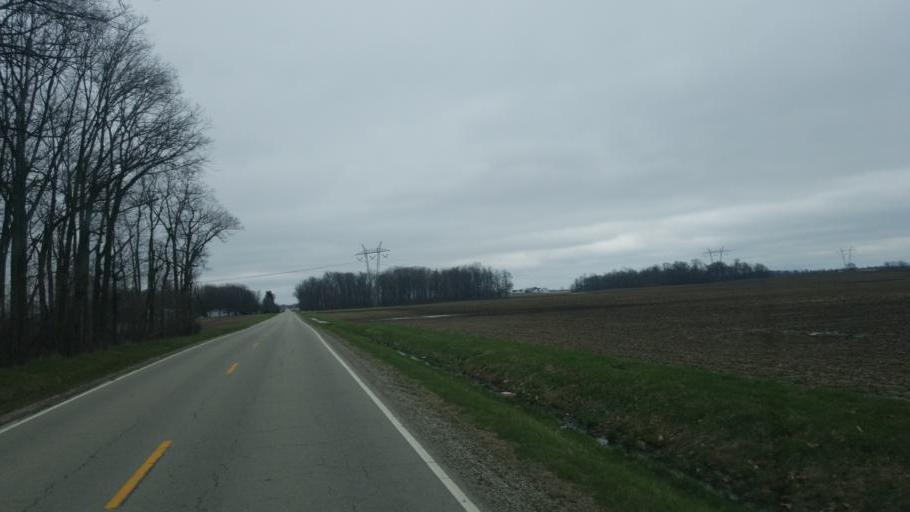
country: US
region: Ohio
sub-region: Crawford County
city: Bucyrus
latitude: 40.8193
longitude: -83.0448
